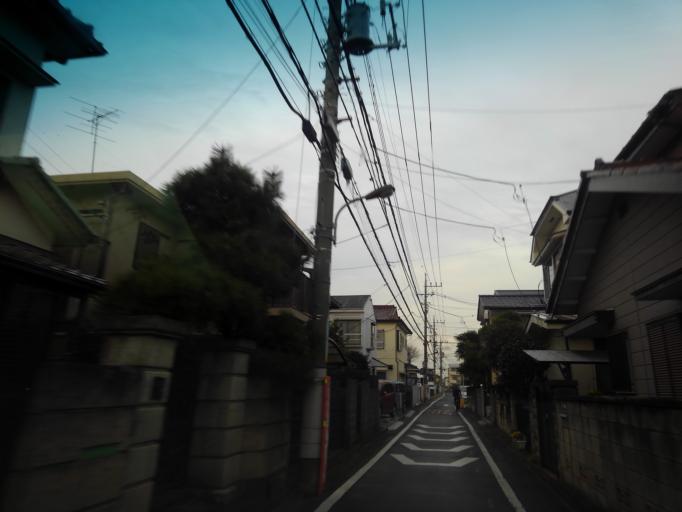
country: JP
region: Tokyo
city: Kokubunji
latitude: 35.7166
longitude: 139.4440
